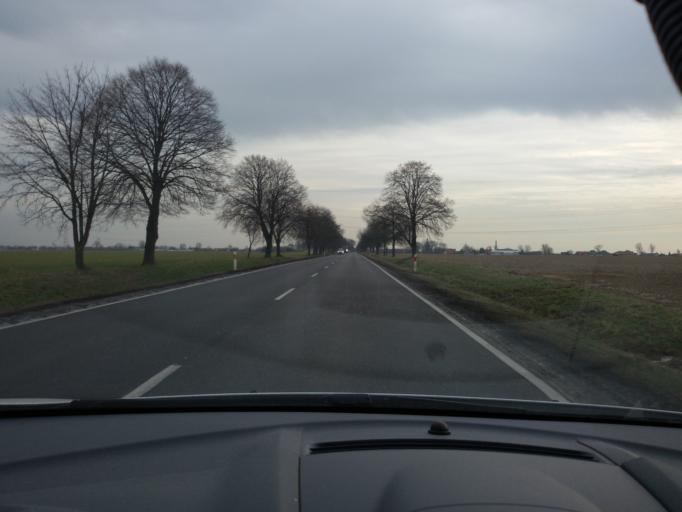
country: PL
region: Greater Poland Voivodeship
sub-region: Powiat leszczynski
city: Swieciechowa
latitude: 51.8238
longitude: 16.4263
